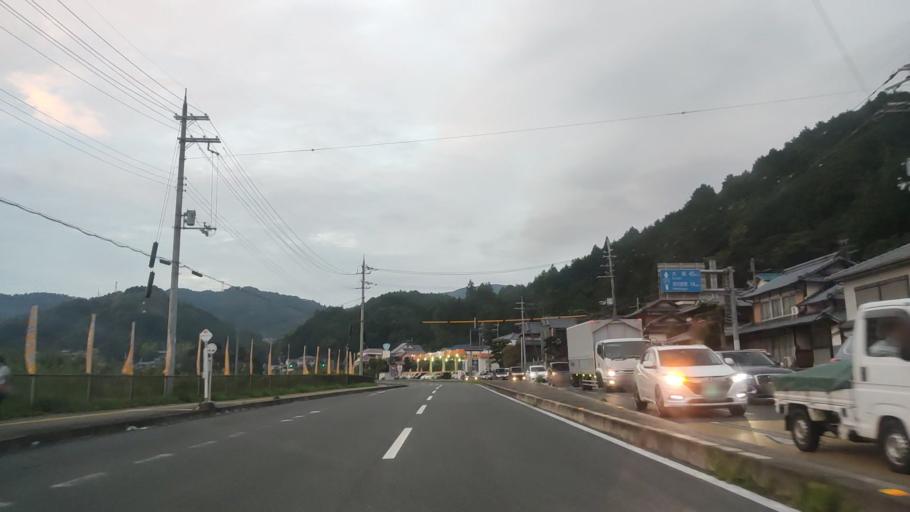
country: JP
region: Wakayama
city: Hashimoto
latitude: 34.3584
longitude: 135.6069
